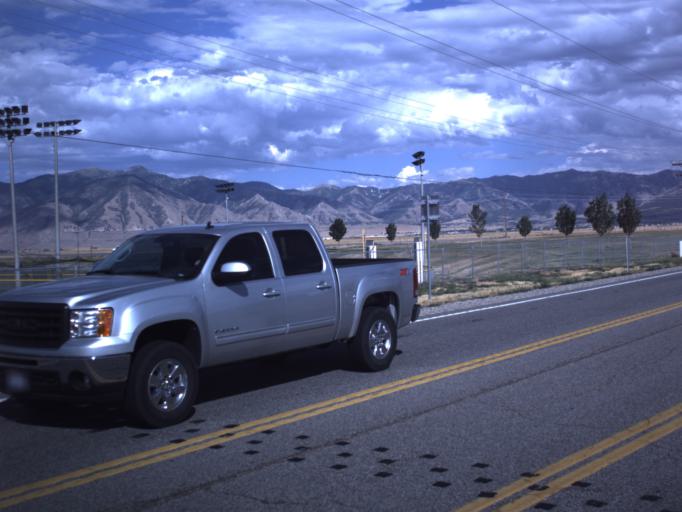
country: US
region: Utah
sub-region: Tooele County
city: Erda
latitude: 40.5676
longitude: -112.3692
